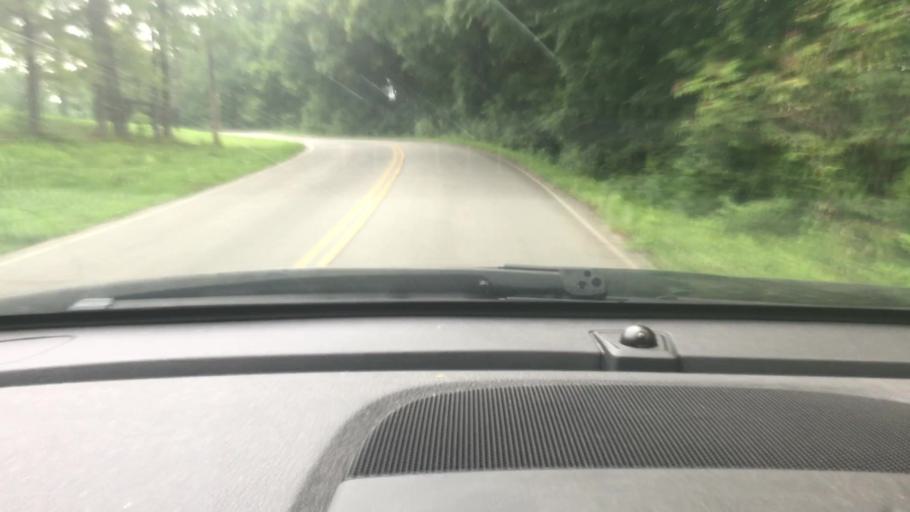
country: US
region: Tennessee
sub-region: Dickson County
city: Charlotte
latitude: 36.1827
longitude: -87.2814
